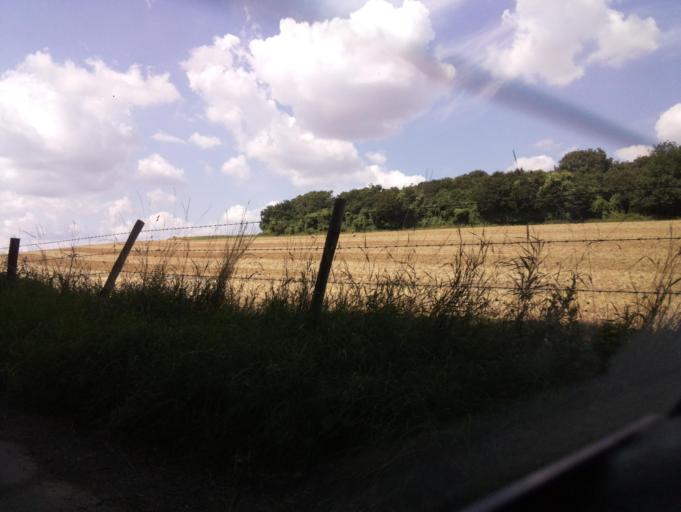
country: GB
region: England
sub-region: West Berkshire
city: Farnborough
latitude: 51.5106
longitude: -1.3678
